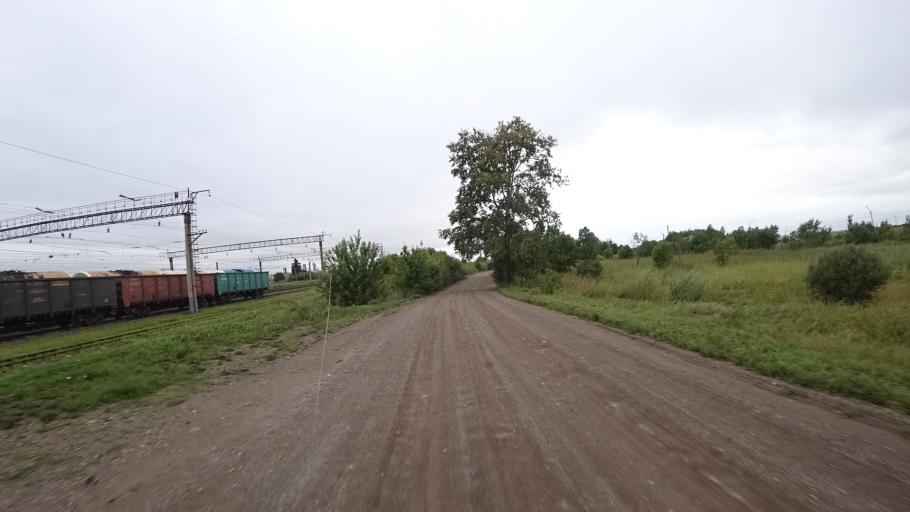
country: RU
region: Primorskiy
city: Chernigovka
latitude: 44.3381
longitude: 132.5297
